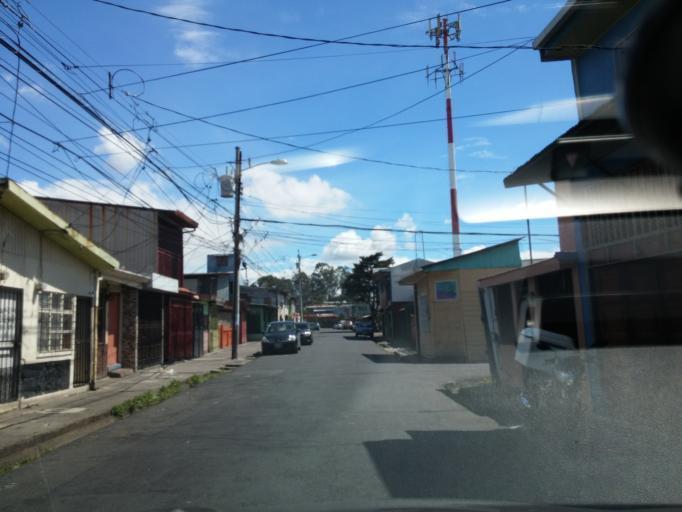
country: CR
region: San Jose
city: San Jose
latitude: 9.9226
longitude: -84.0913
